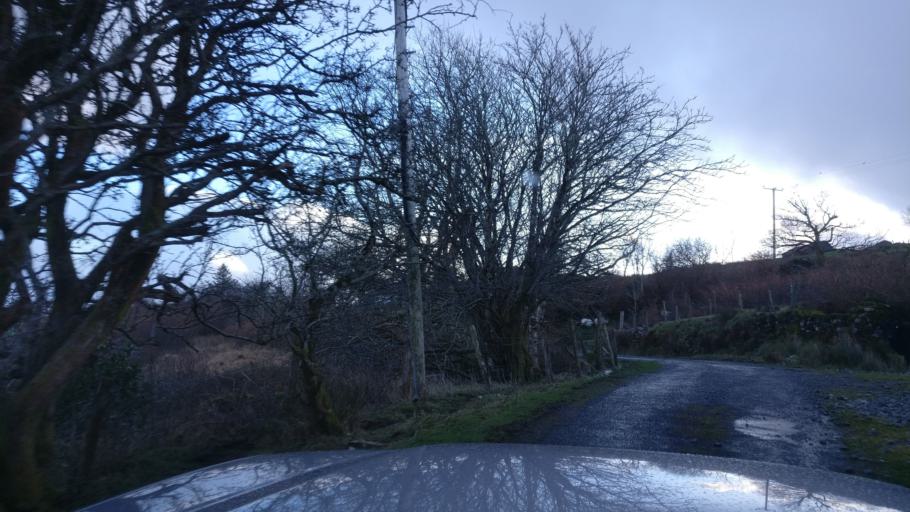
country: IE
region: Connaught
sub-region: County Galway
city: Clifden
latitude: 53.4877
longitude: -9.6983
